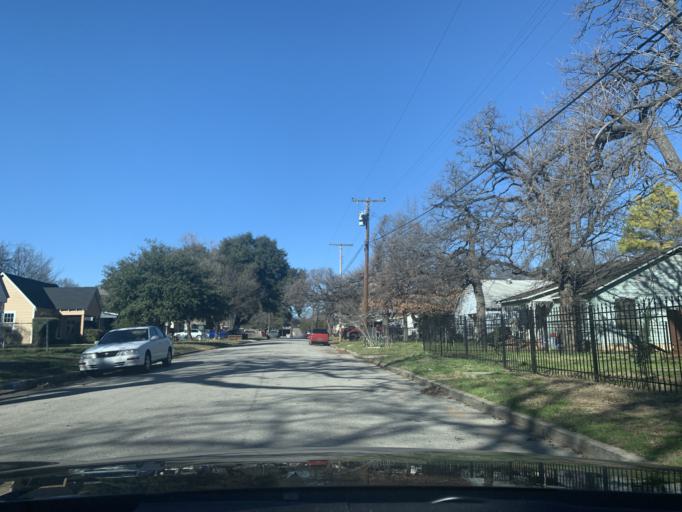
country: US
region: Texas
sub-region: Tarrant County
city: Haltom City
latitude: 32.7798
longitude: -97.2819
